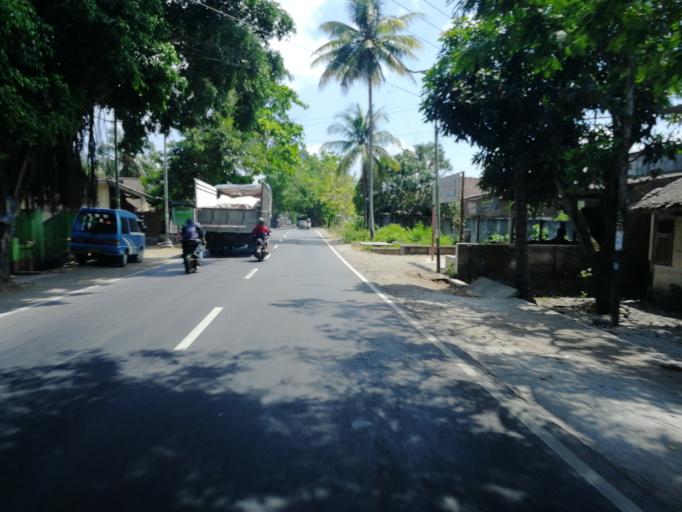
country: ID
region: West Nusa Tenggara
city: Jelateng Timur
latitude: -8.7131
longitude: 116.0757
